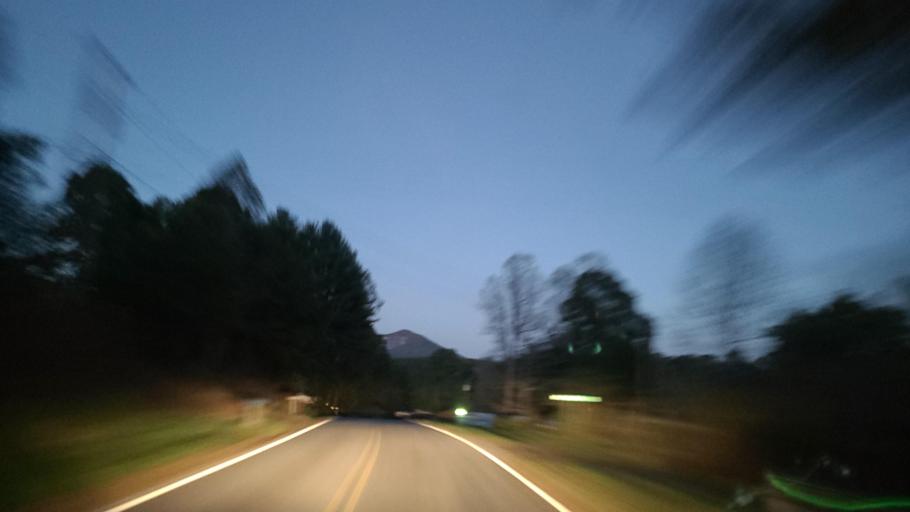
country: US
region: North Carolina
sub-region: Clay County
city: Hayesville
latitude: 34.9691
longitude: -83.8854
